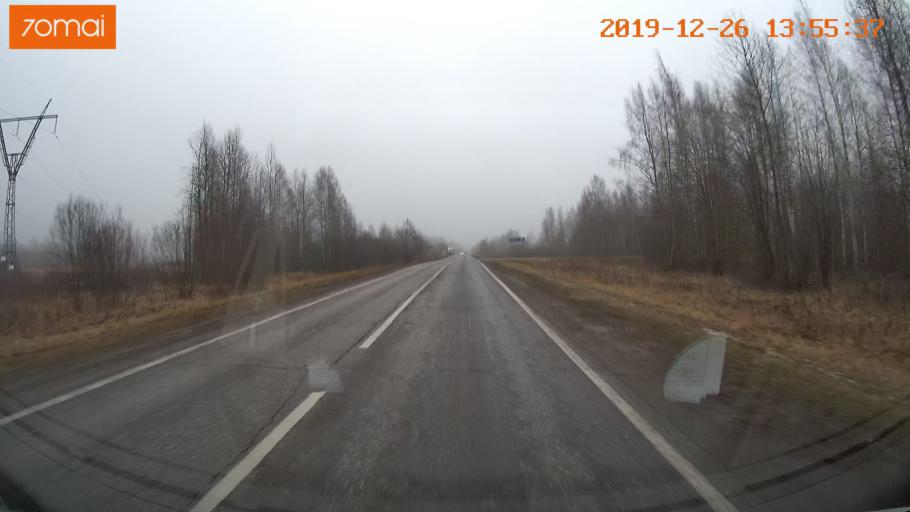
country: RU
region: Jaroslavl
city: Poshekhon'ye
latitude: 58.6014
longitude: 38.6492
